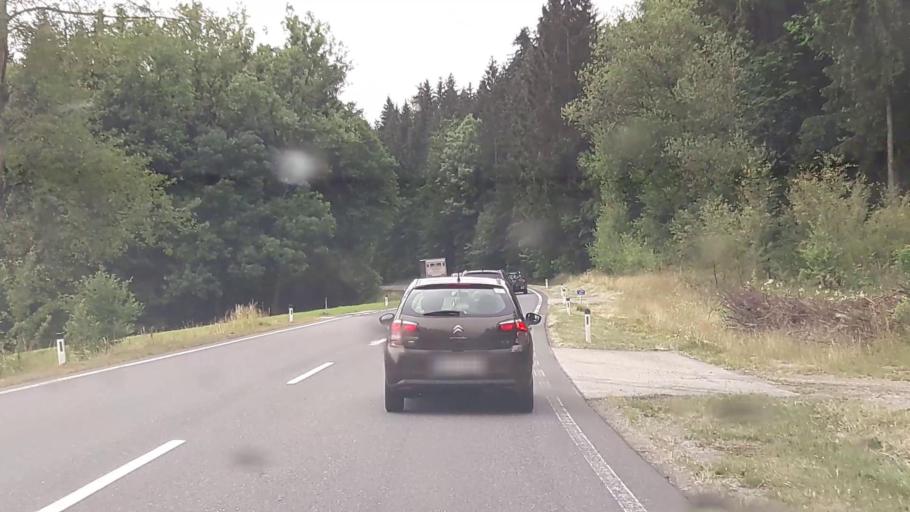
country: AT
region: Upper Austria
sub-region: Politischer Bezirk Rohrbach
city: Kleinzell im Muehlkreis
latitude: 48.4533
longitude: 14.0349
